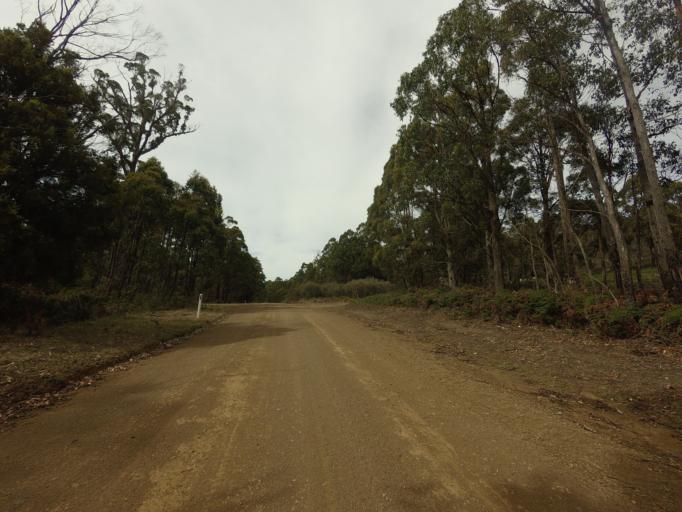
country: AU
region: Tasmania
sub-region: Sorell
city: Sorell
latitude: -42.4853
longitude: 147.6170
